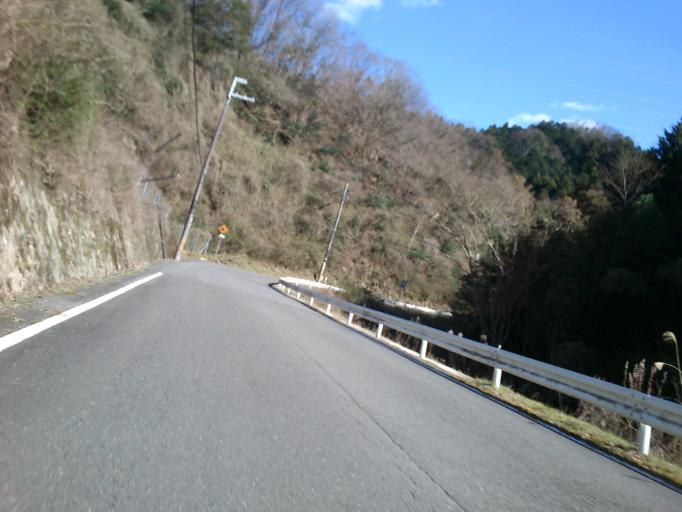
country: JP
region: Kyoto
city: Tanabe
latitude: 34.8037
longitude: 135.8473
